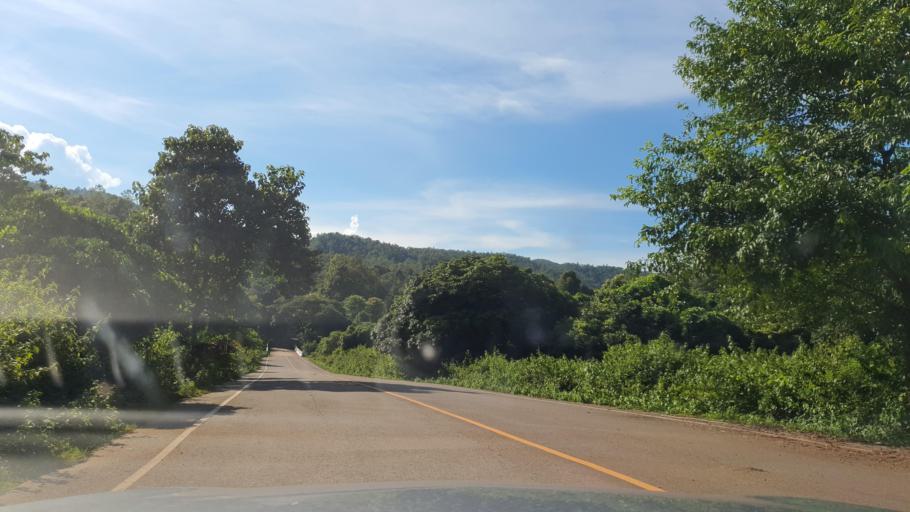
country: TH
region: Chiang Mai
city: Mae On
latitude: 18.7498
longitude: 99.3030
